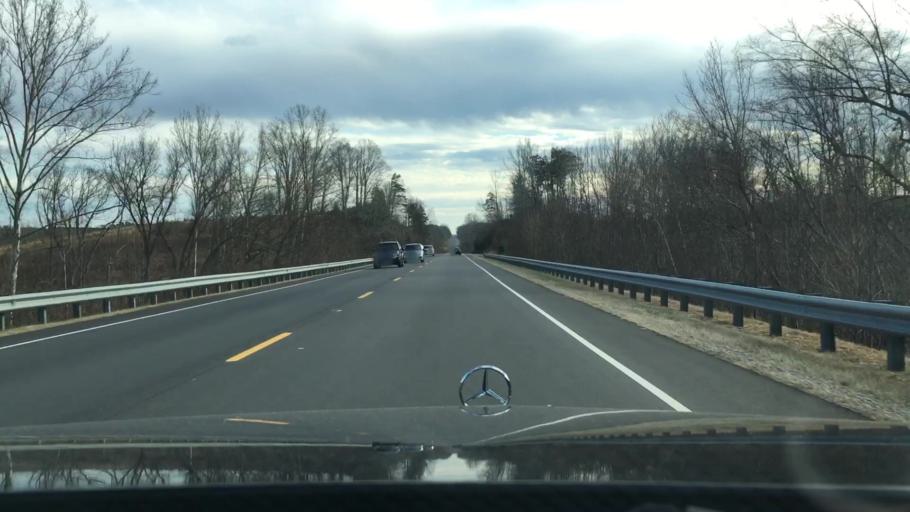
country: US
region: Virginia
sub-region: City of Danville
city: Danville
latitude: 36.5120
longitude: -79.3916
